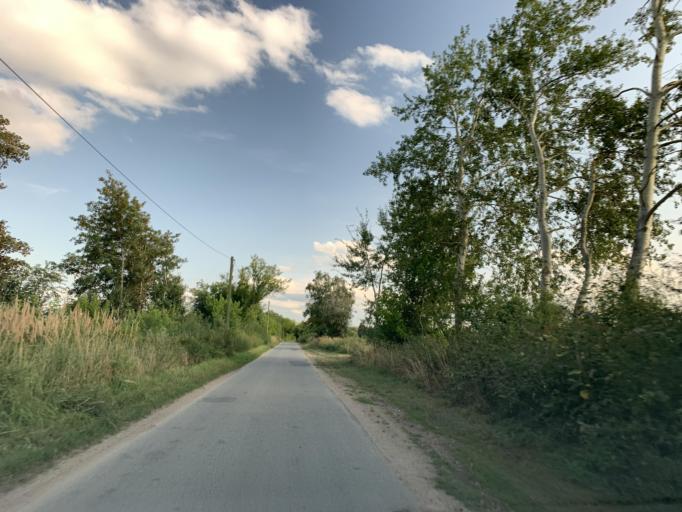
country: DE
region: Mecklenburg-Vorpommern
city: Loitz
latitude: 53.3603
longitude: 13.3490
